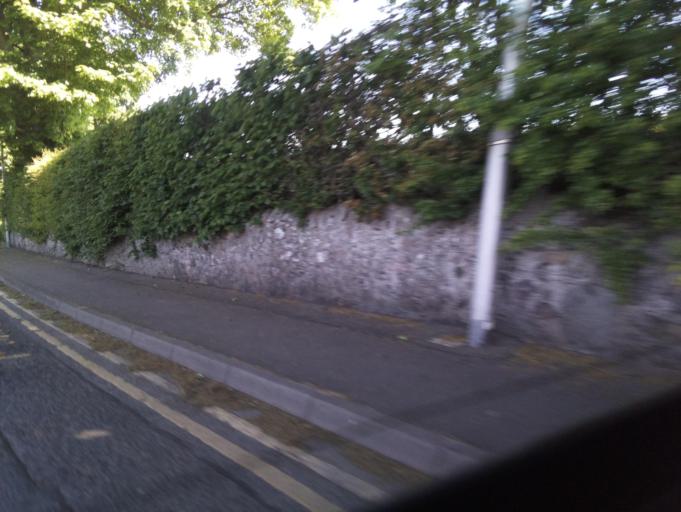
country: GB
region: Scotland
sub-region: Fife
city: Newport-On-Tay
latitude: 56.4308
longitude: -2.9361
